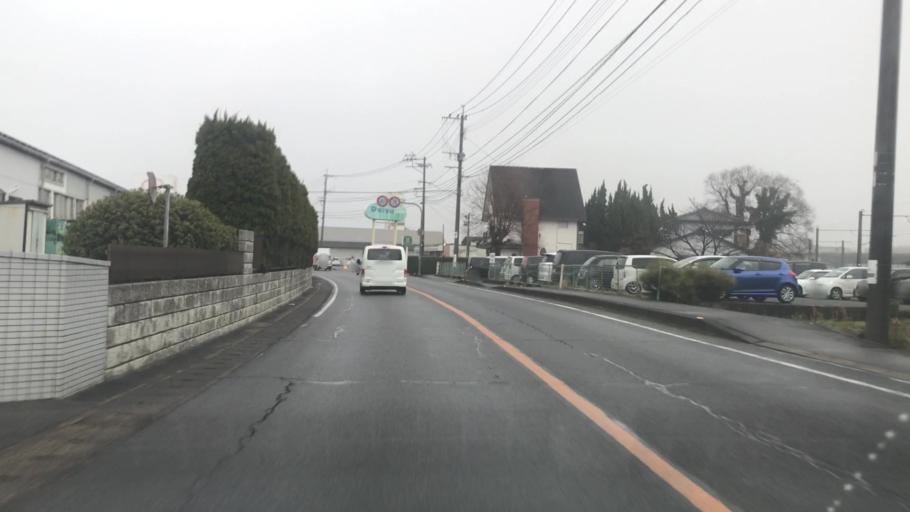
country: JP
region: Saga Prefecture
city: Takeocho-takeo
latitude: 33.2108
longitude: 130.0461
